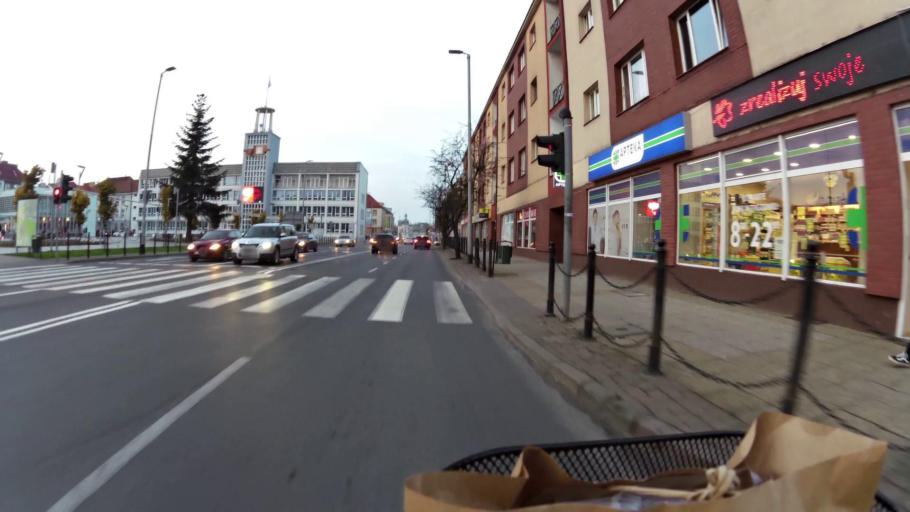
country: PL
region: West Pomeranian Voivodeship
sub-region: Koszalin
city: Koszalin
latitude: 54.1902
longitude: 16.1825
